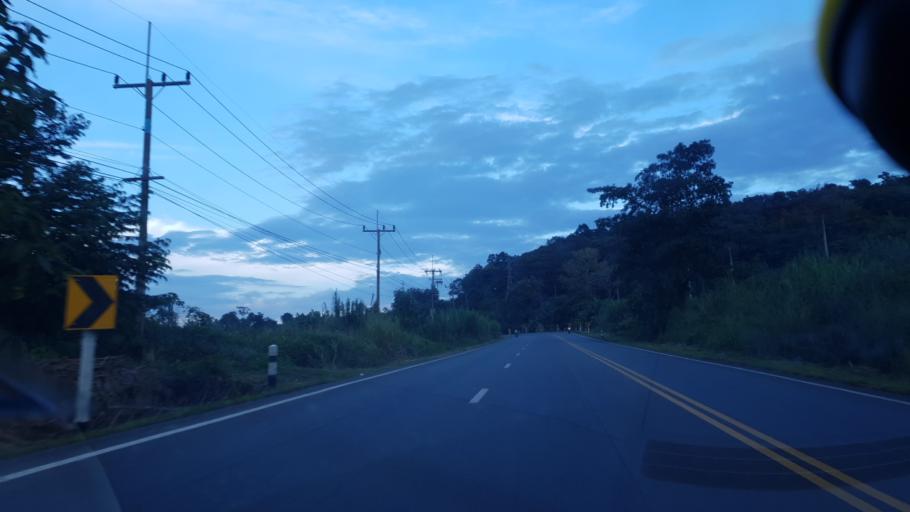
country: TH
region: Chiang Rai
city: Mae Lao
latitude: 19.7325
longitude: 99.6253
